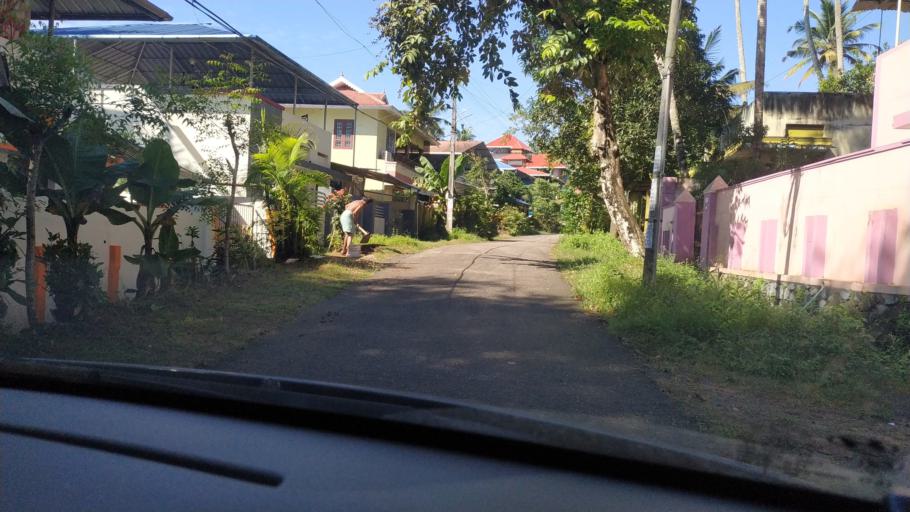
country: IN
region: Kerala
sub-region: Thiruvananthapuram
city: Nedumangad
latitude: 8.6073
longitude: 76.9962
